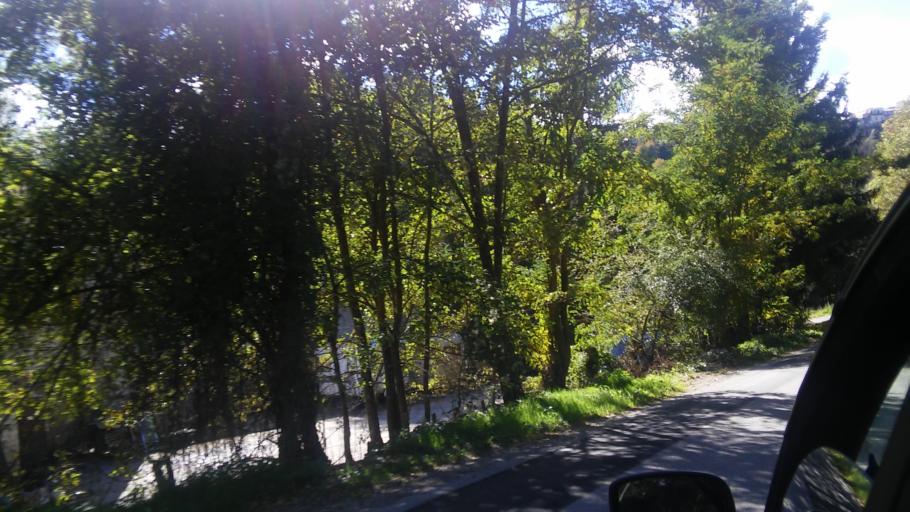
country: IT
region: Latium
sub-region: Provincia di Rieti
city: Amatrice
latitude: 42.6326
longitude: 13.2947
